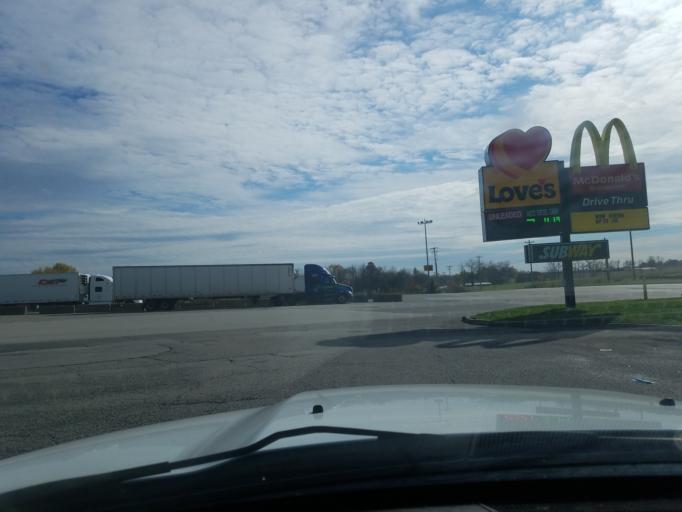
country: US
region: Indiana
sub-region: Clark County
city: Henryville
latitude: 38.4895
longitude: -85.7698
